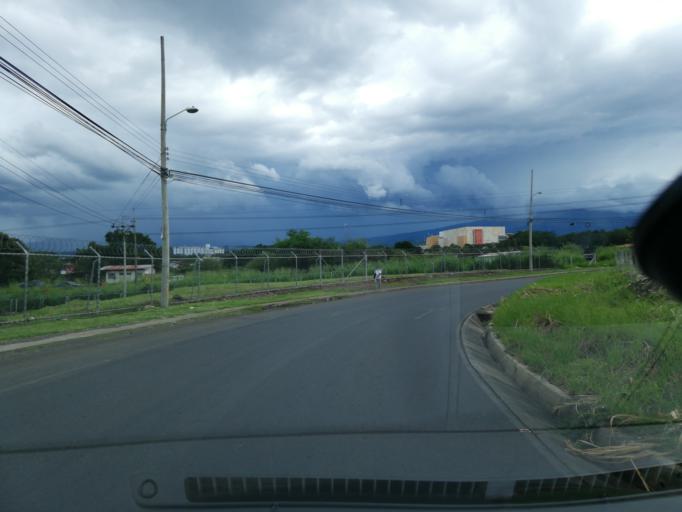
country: CR
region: Alajuela
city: Alajuela
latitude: 9.9978
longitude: -84.2152
